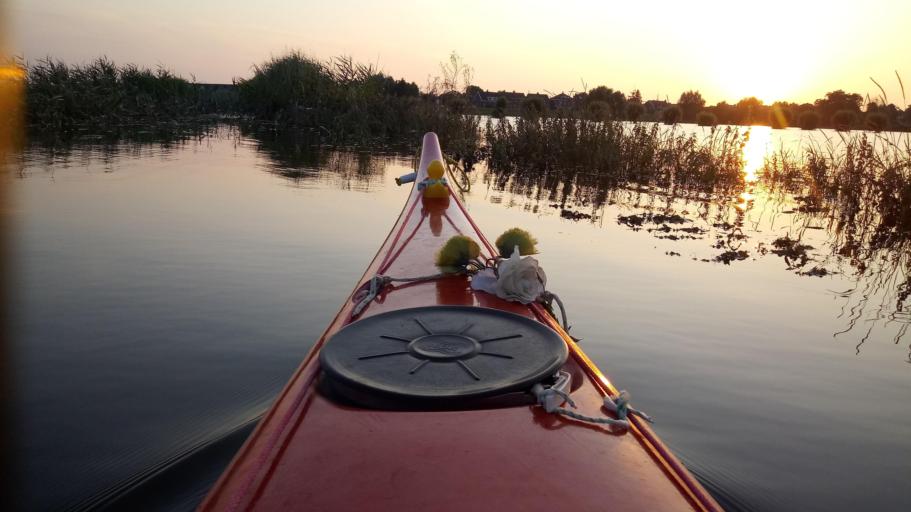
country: NL
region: Gelderland
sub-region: Gemeente Zutphen
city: Zutphen
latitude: 52.1360
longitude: 6.1890
